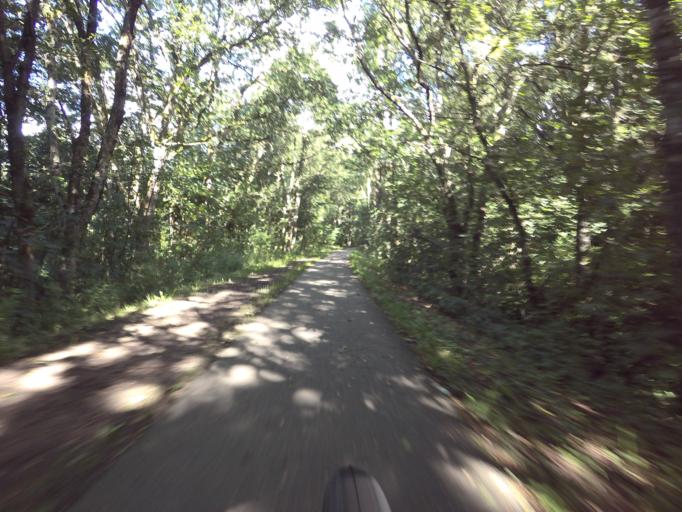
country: DK
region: Central Jutland
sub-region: Horsens Kommune
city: Braedstrup
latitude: 55.9697
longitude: 9.6915
